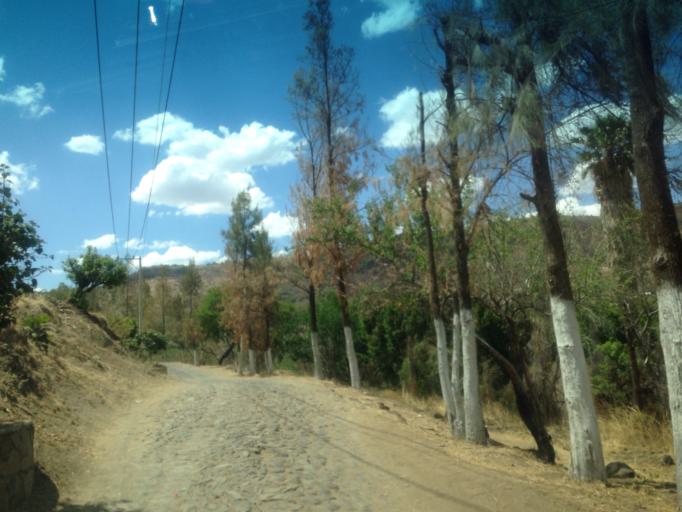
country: MX
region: Jalisco
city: Atotonilco el Alto
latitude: 20.5628
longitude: -102.5129
